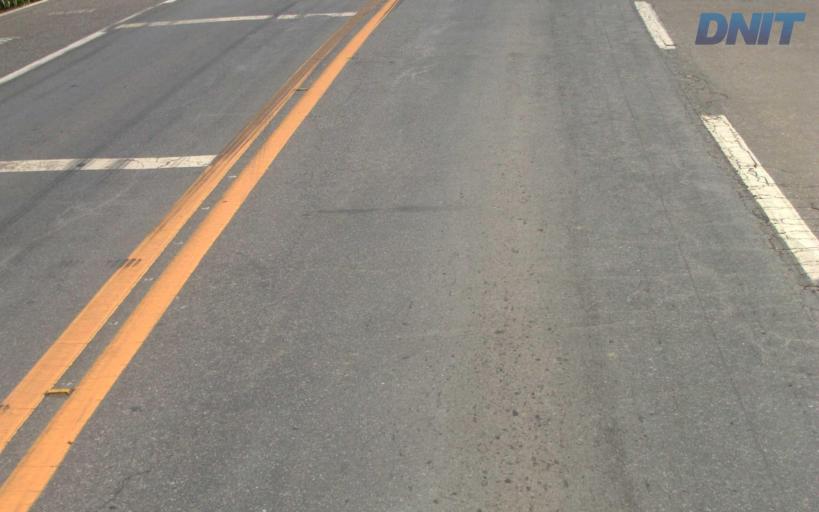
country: BR
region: Minas Gerais
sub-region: Governador Valadares
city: Governador Valadares
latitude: -18.9559
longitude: -42.0758
